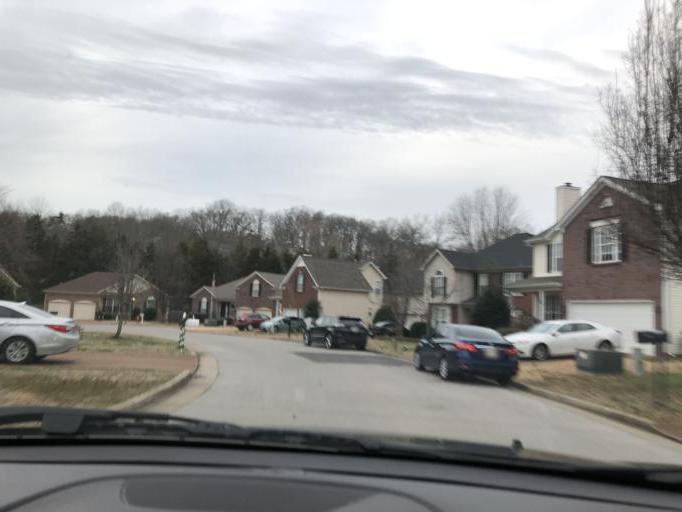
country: US
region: Tennessee
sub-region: Wilson County
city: Green Hill
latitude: 36.2010
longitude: -86.5971
